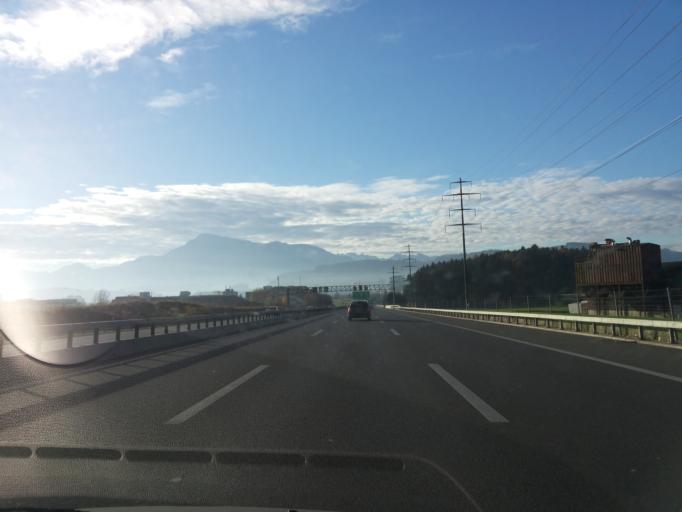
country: CH
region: Zug
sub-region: Zug
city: Hunenberg
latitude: 47.1665
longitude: 8.4323
